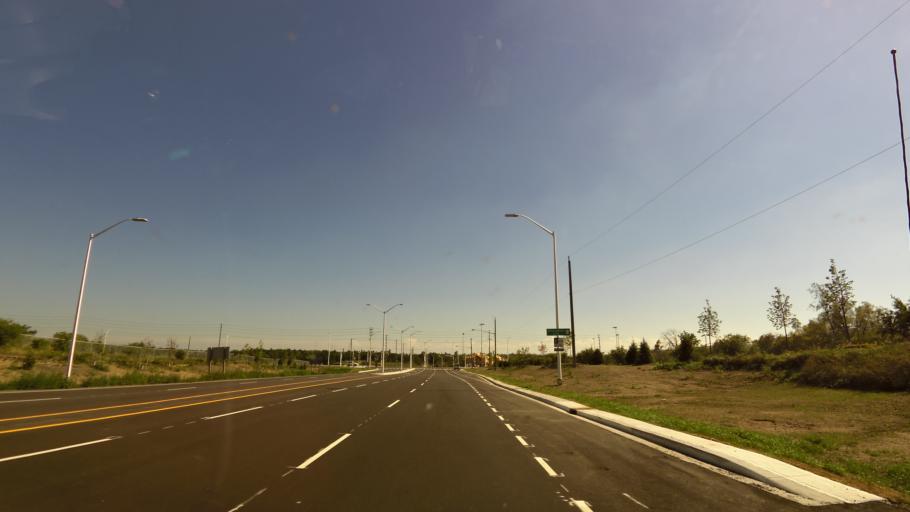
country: CA
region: Ontario
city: Oakville
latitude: 43.4818
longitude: -79.7629
